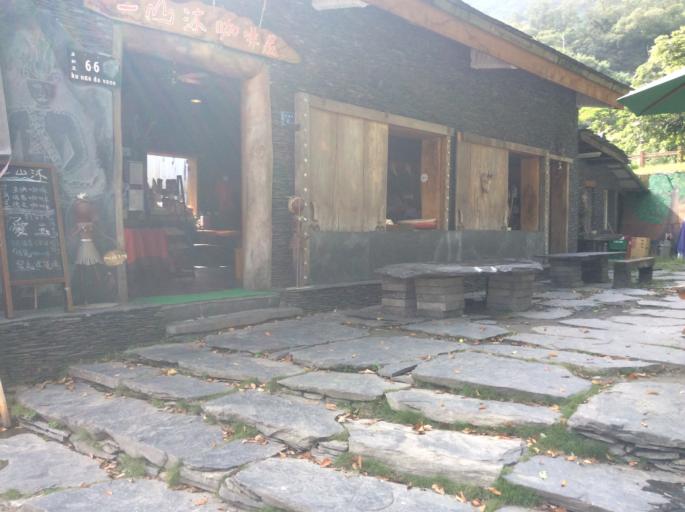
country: TW
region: Taiwan
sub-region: Pingtung
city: Pingtung
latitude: 22.9096
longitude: 120.7145
